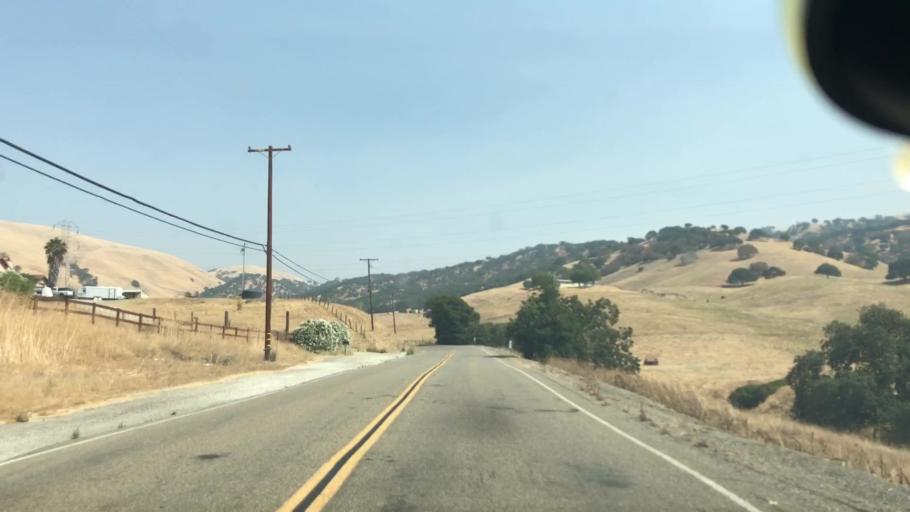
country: US
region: California
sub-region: Alameda County
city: Livermore
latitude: 37.6442
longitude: -121.6462
